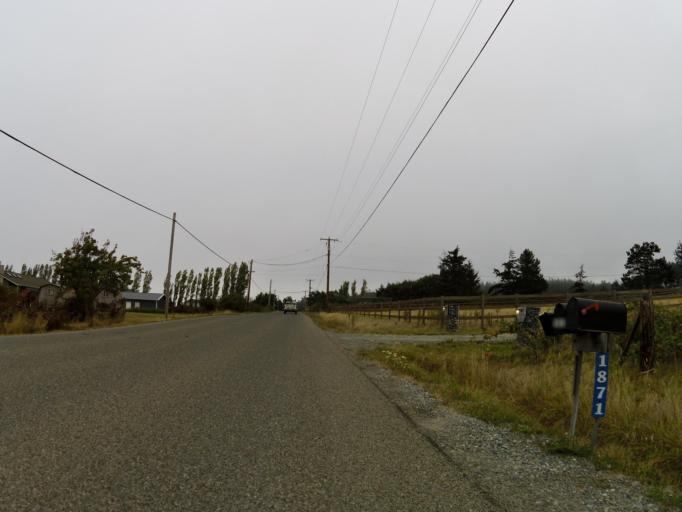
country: US
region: Washington
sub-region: Island County
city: Ault Field
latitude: 48.3034
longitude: -122.7129
